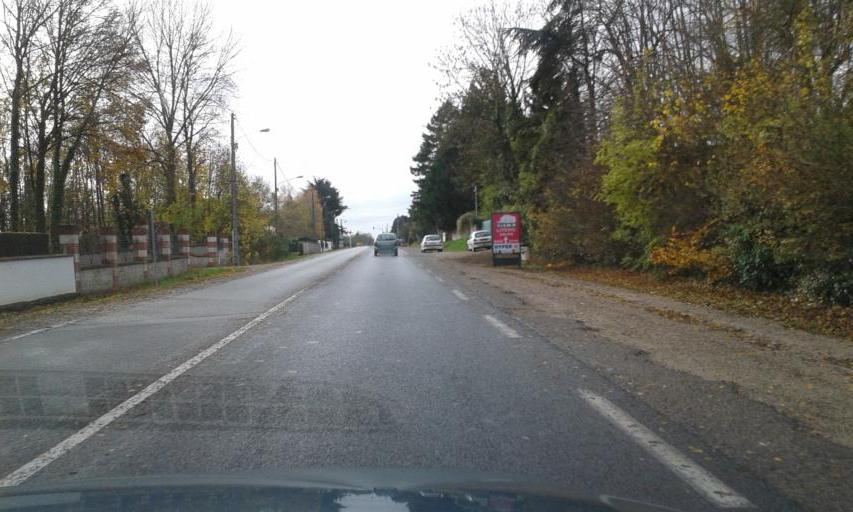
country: FR
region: Centre
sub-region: Departement du Loiret
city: Saint-Ay
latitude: 47.8559
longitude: 1.7484
